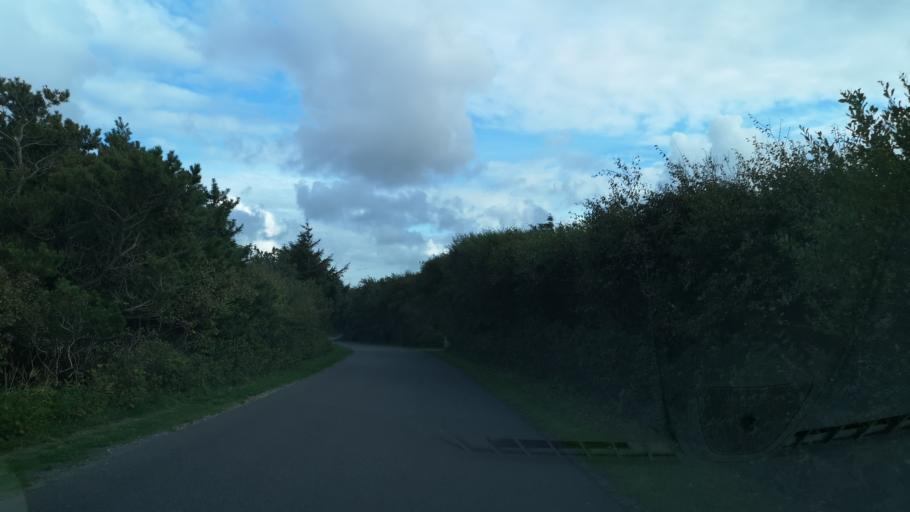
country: DK
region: Central Jutland
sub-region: Ringkobing-Skjern Kommune
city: Hvide Sande
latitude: 56.1241
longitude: 8.1292
